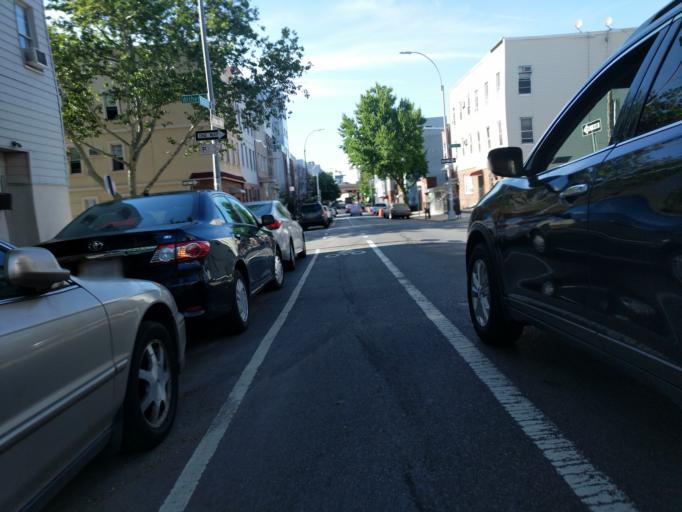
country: US
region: New York
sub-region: Queens County
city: Long Island City
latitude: 40.7170
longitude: -73.9465
